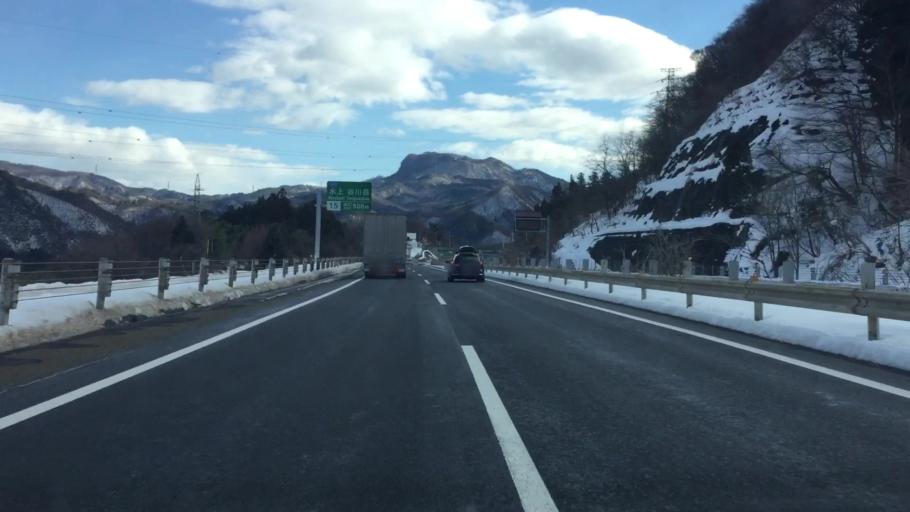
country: JP
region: Gunma
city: Numata
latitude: 36.7524
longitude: 138.9697
